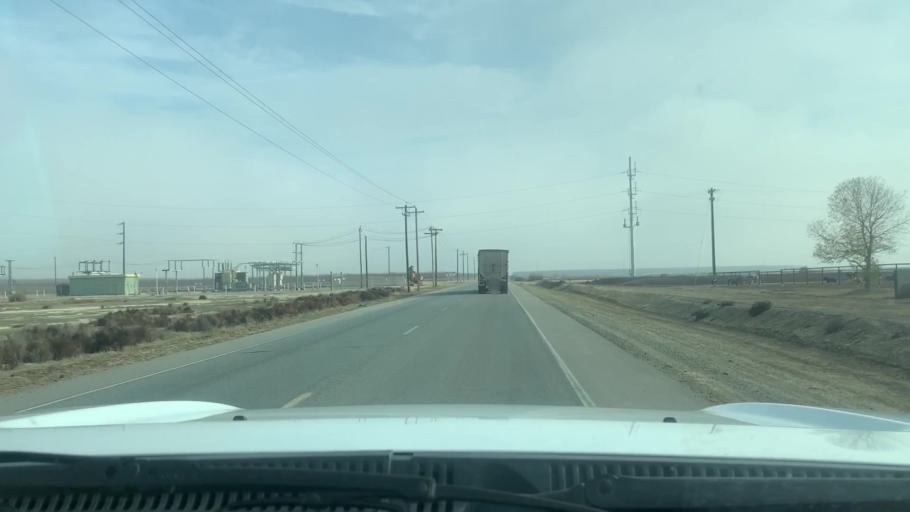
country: US
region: California
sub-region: Kern County
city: Buttonwillow
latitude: 35.5005
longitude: -119.4504
